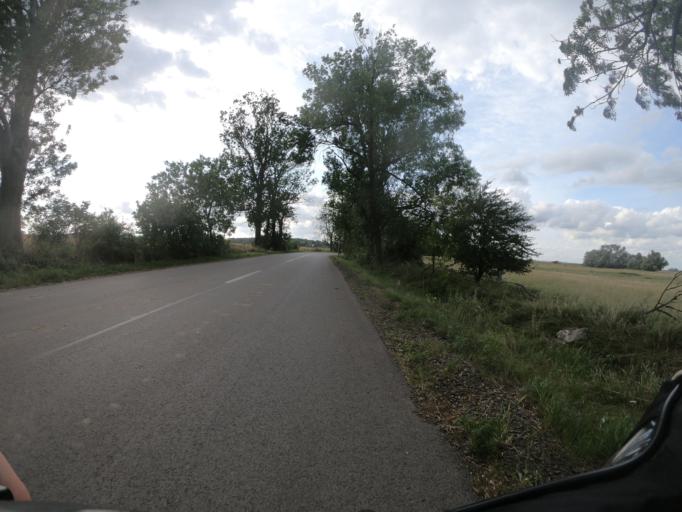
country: HU
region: Borsod-Abauj-Zemplen
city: Mezocsat
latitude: 47.8226
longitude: 20.8515
